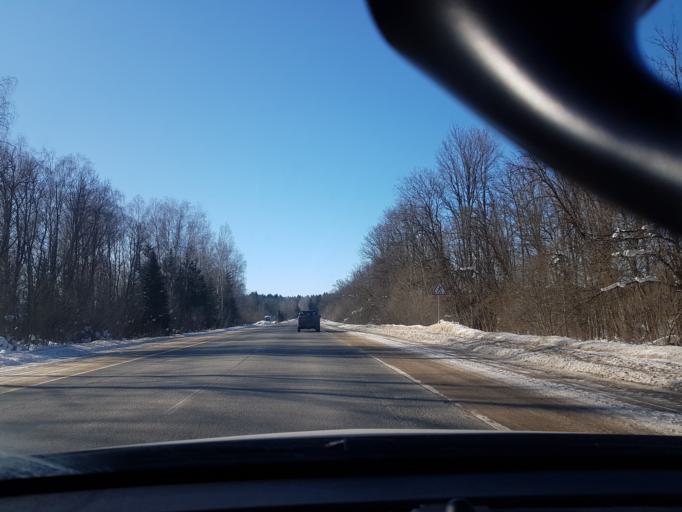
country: RU
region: Moskovskaya
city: Kostrovo
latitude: 55.9183
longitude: 36.6727
